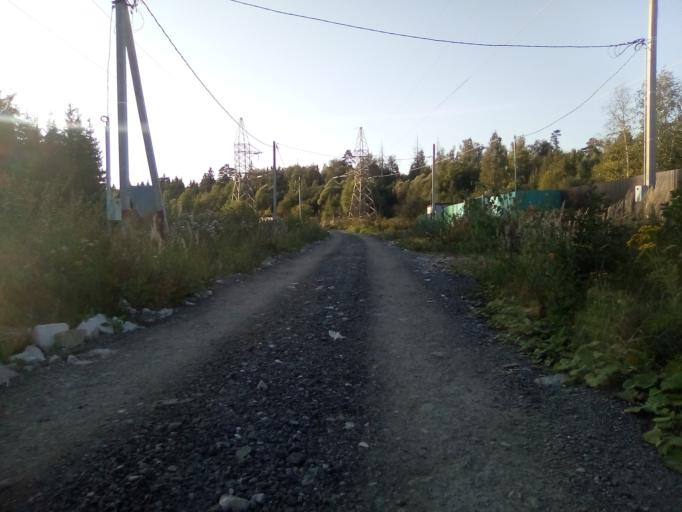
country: RU
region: Moskovskaya
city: Aprelevka
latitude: 55.5799
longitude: 37.0647
